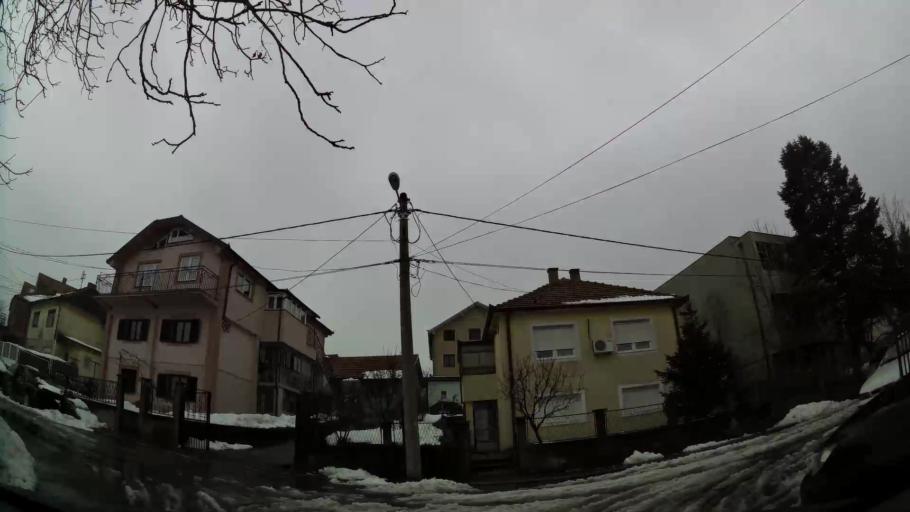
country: RS
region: Central Serbia
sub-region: Belgrade
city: Zvezdara
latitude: 44.7466
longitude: 20.5036
